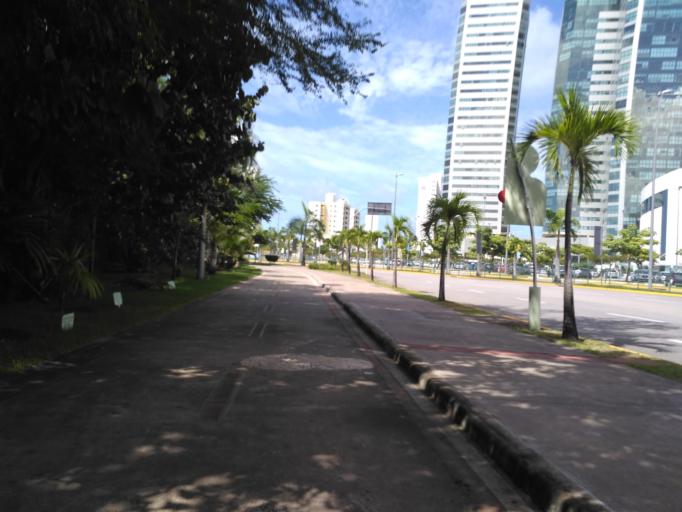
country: BR
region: Pernambuco
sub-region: Recife
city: Recife
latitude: -8.0850
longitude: -34.8934
